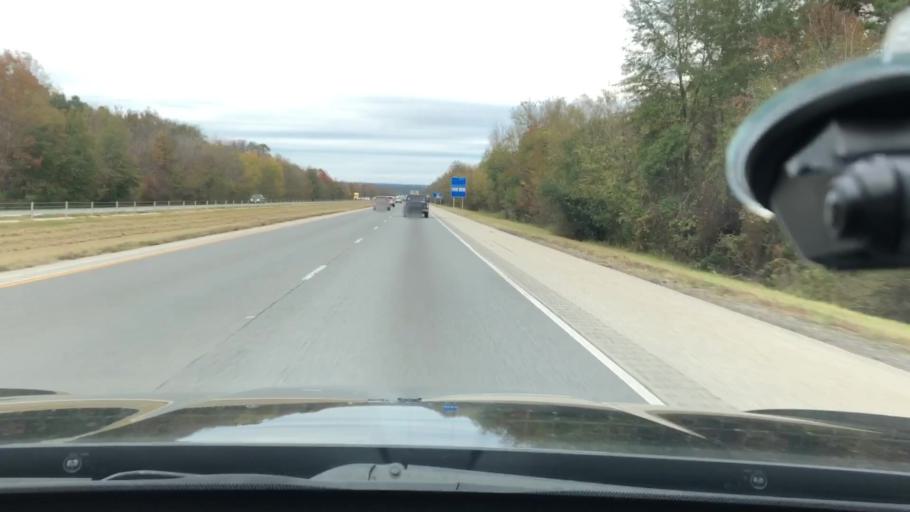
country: US
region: Arkansas
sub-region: Clark County
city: Arkadelphia
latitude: 34.1549
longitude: -93.0777
